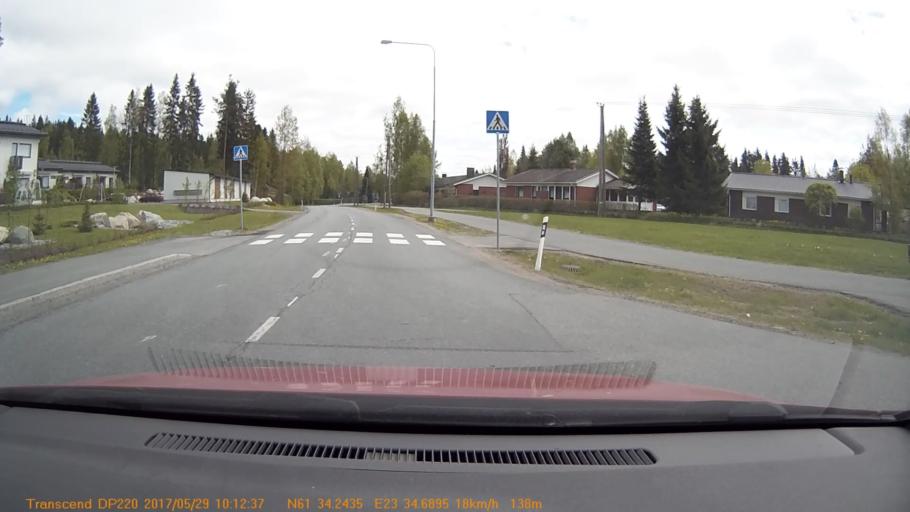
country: FI
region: Pirkanmaa
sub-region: Tampere
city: Yloejaervi
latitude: 61.5707
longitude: 23.5780
